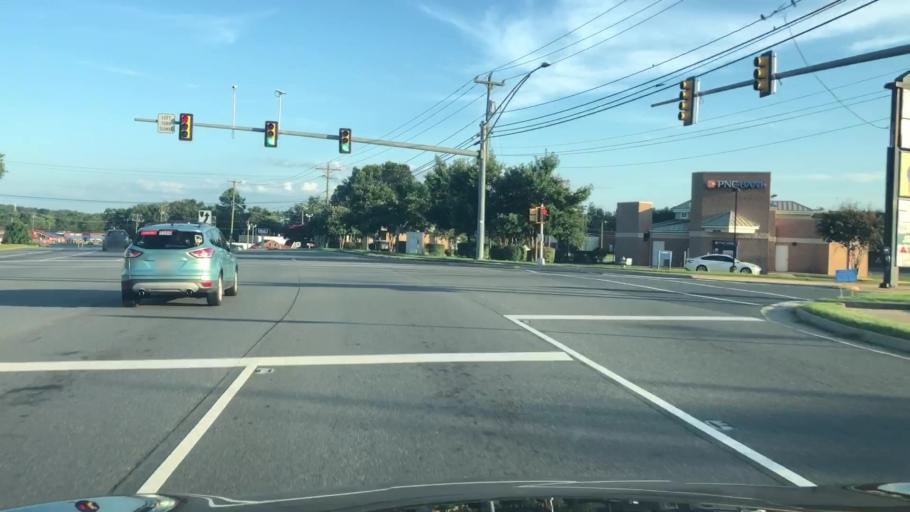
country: US
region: Virginia
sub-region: City of Fredericksburg
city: Fredericksburg
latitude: 38.3137
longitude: -77.4514
